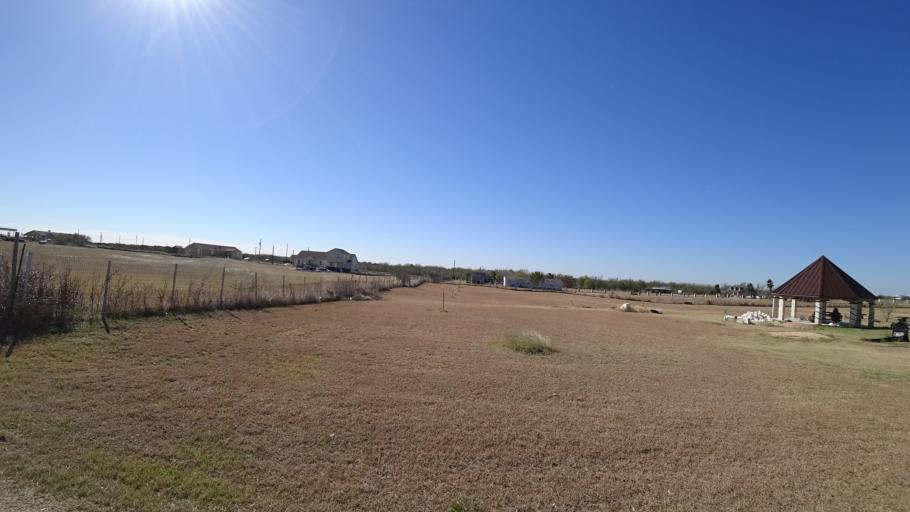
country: US
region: Texas
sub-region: Travis County
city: Garfield
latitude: 30.0992
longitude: -97.6193
